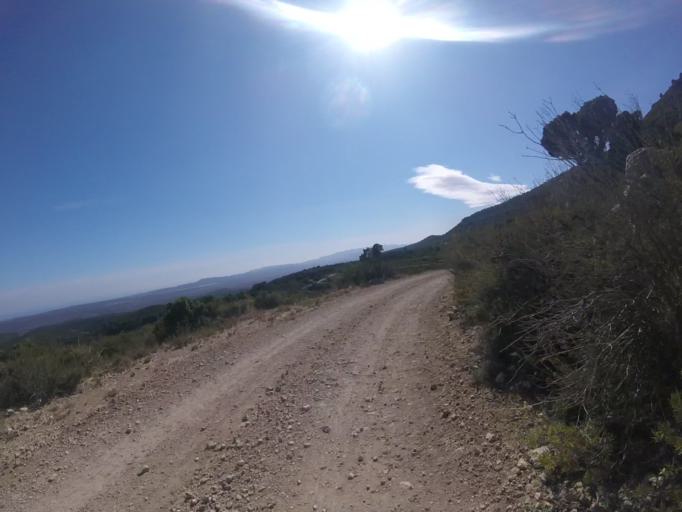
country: ES
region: Valencia
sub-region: Provincia de Castello
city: Sierra-Engarceran
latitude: 40.2737
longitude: 0.0072
